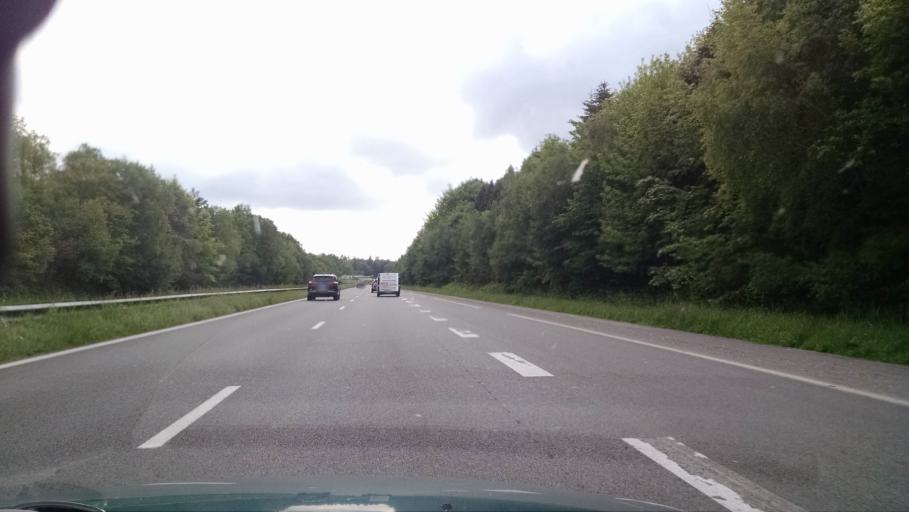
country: FR
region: Brittany
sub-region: Departement du Finistere
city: Morlaix
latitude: 48.5882
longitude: -3.7988
